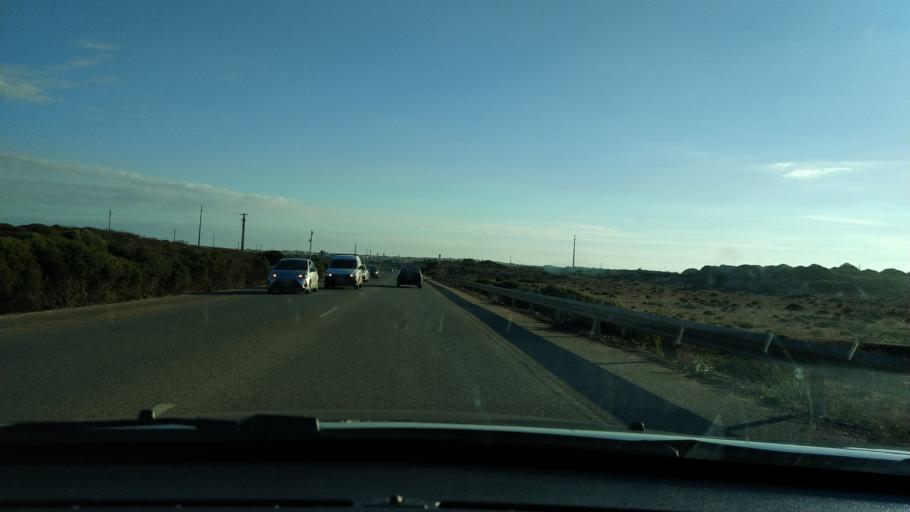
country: PT
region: Faro
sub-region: Vila do Bispo
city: Sagres
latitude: 37.0290
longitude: -8.9366
